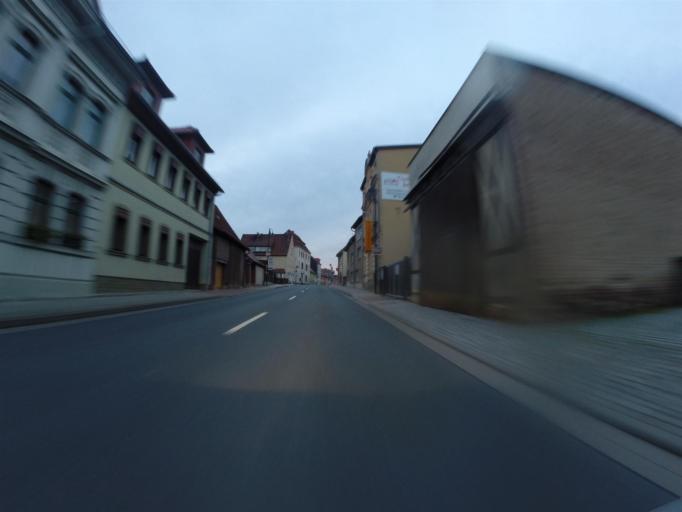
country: DE
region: Thuringia
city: Burgel
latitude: 50.9424
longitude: 11.7586
